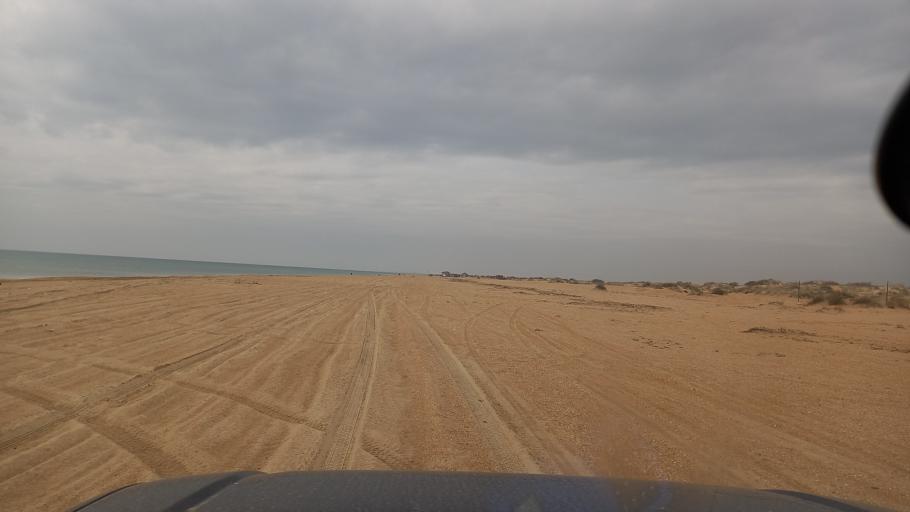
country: RU
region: Krasnodarskiy
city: Vityazevo
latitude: 44.9922
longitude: 37.2306
